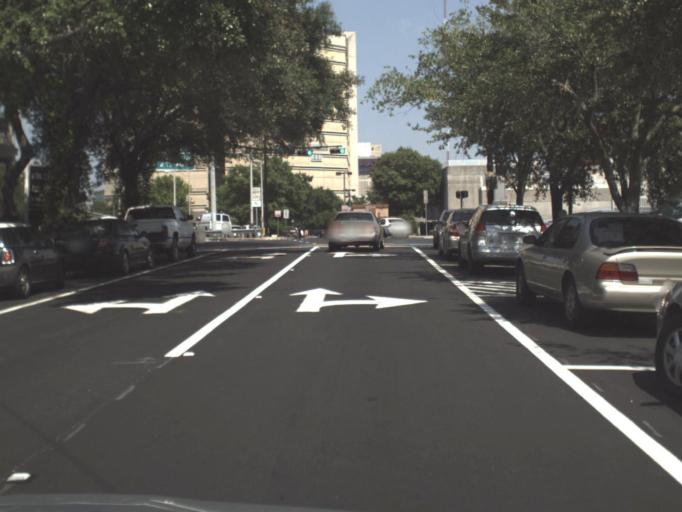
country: US
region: Florida
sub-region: Duval County
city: Jacksonville
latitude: 30.3260
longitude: -81.6532
